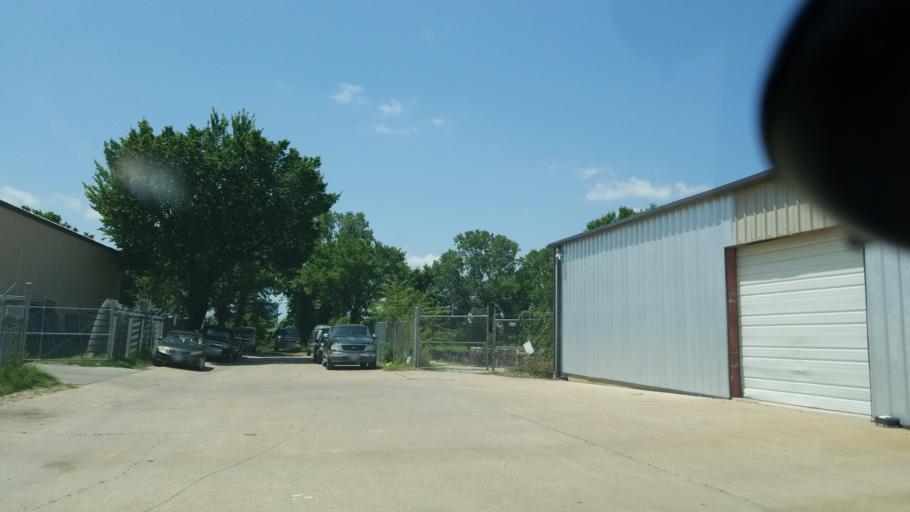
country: US
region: Texas
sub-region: Dallas County
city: University Park
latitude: 32.8257
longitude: -96.8607
